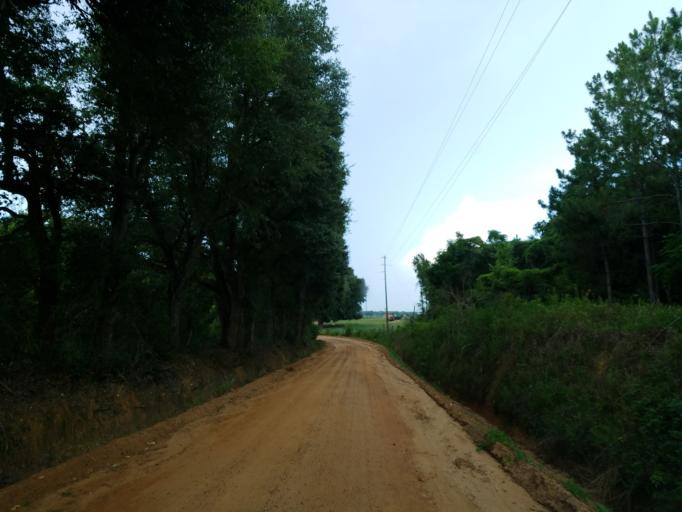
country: US
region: Georgia
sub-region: Tift County
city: Omega
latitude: 31.2743
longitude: -83.5227
